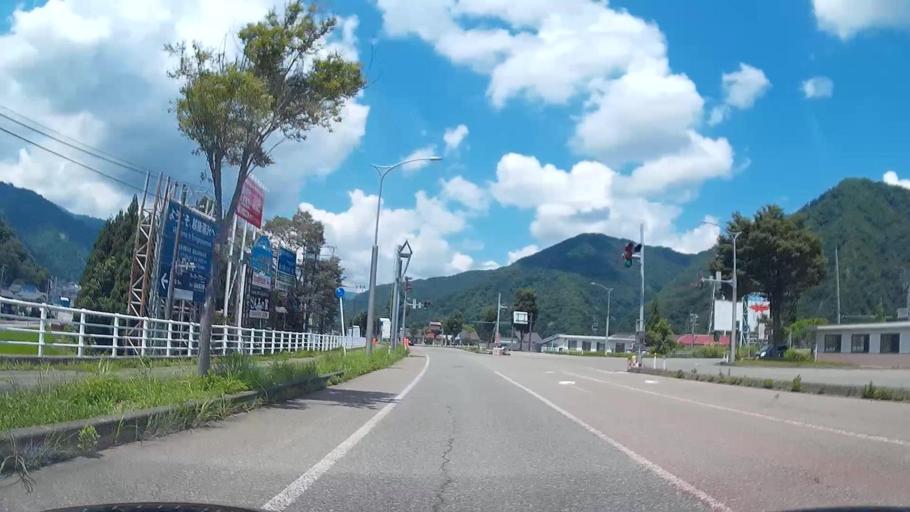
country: JP
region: Niigata
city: Shiozawa
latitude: 36.9296
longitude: 138.8237
